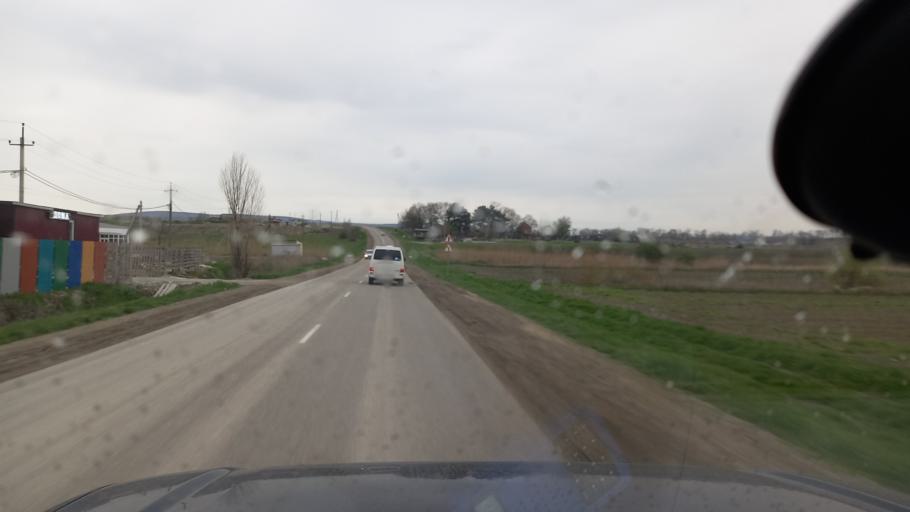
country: RU
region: Krasnodarskiy
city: Anapskaya
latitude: 44.8871
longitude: 37.4560
